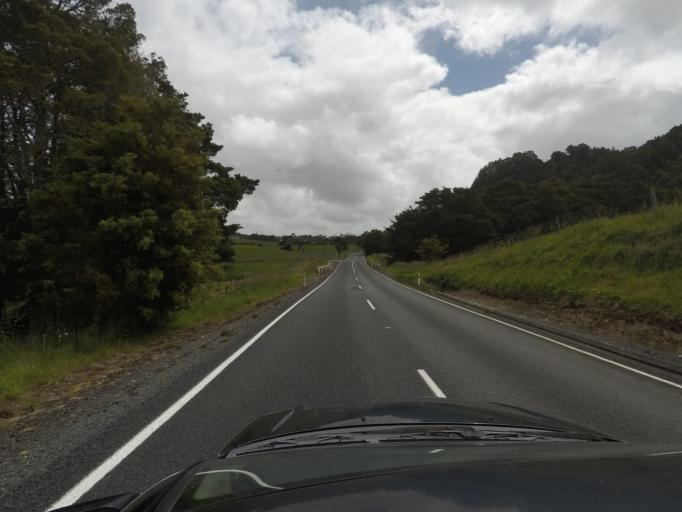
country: NZ
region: Auckland
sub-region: Auckland
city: Warkworth
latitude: -36.5015
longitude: 174.5263
